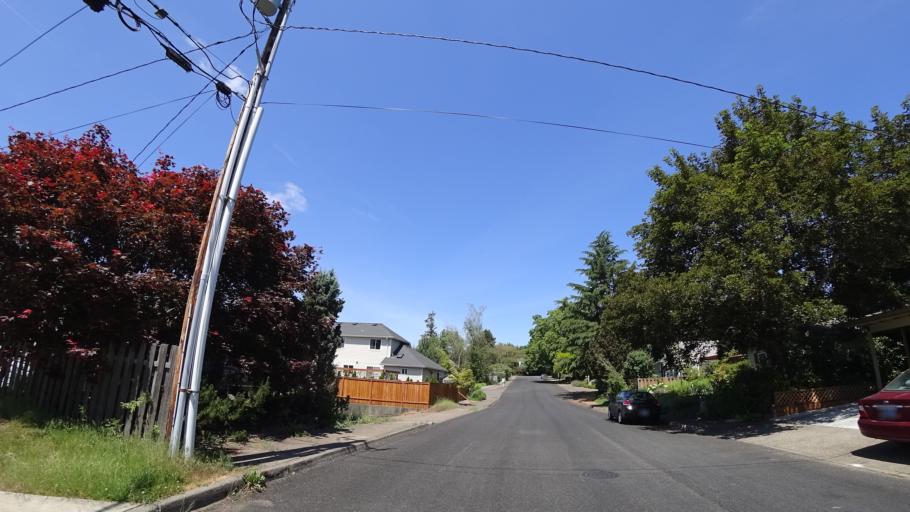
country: US
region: Oregon
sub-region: Washington County
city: Tigard
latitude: 45.4376
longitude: -122.8043
